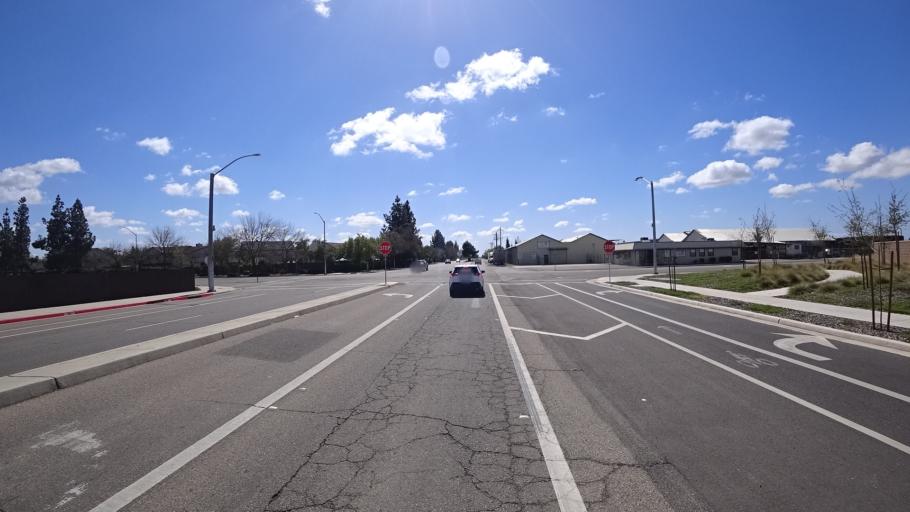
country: US
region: California
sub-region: Fresno County
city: West Park
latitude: 36.7867
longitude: -119.8893
